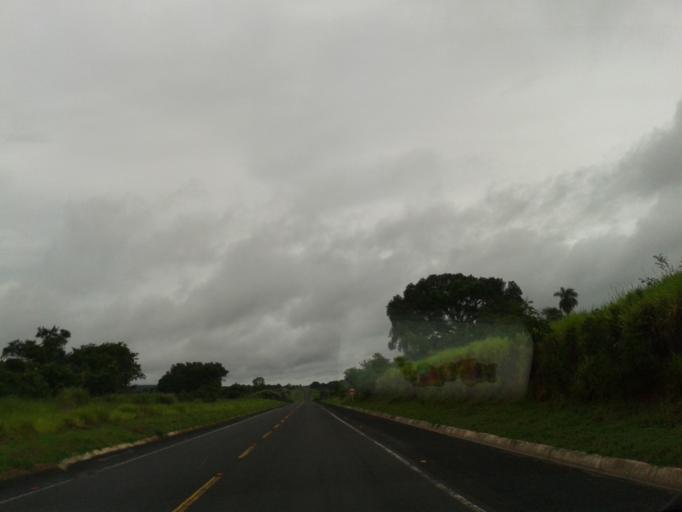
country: BR
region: Minas Gerais
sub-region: Santa Vitoria
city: Santa Vitoria
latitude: -19.2484
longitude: -50.0124
